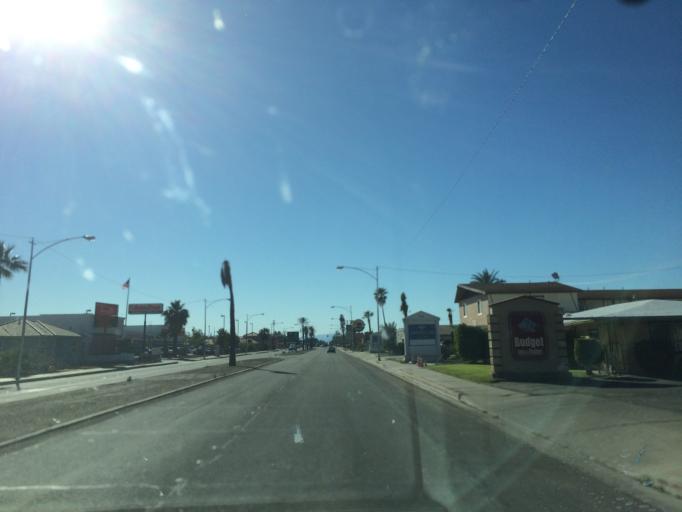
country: US
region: California
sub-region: Imperial County
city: El Centro
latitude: 32.7966
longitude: -115.5657
